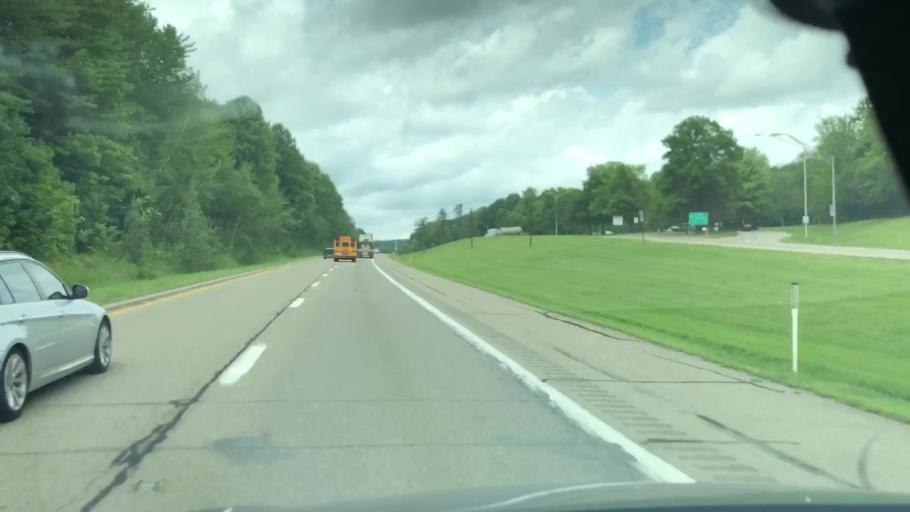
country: US
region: Pennsylvania
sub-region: Erie County
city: Edinboro
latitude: 41.8402
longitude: -80.1759
